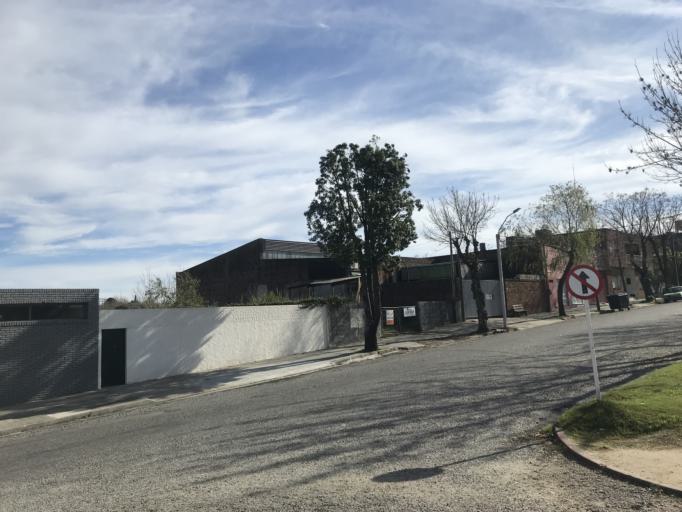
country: UY
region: Colonia
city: Colonia del Sacramento
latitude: -34.4691
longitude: -57.8393
